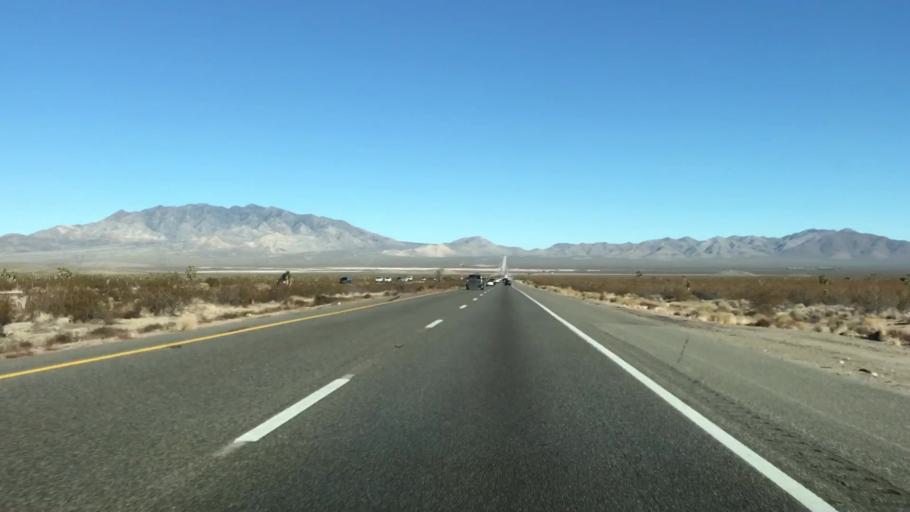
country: US
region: Nevada
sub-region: Clark County
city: Sandy Valley
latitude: 35.4177
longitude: -115.7481
